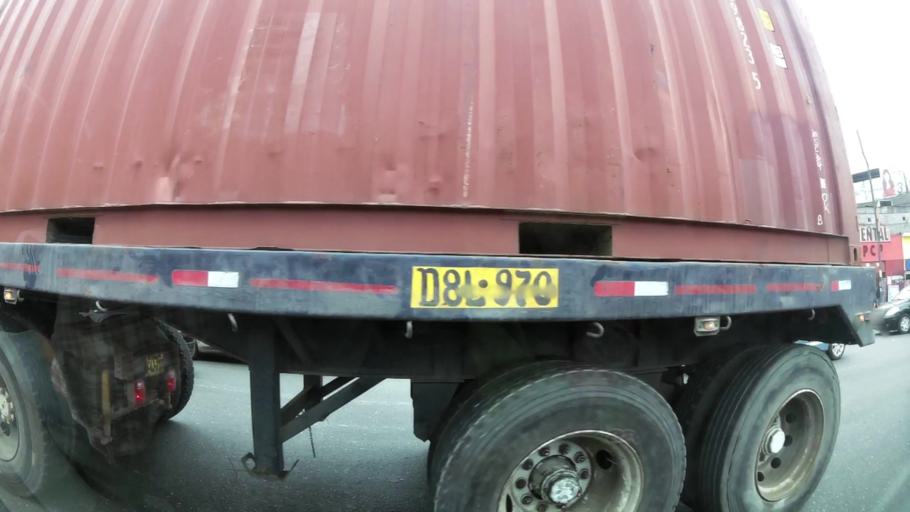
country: PE
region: Lima
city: Lima
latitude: -12.0431
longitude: -77.0425
